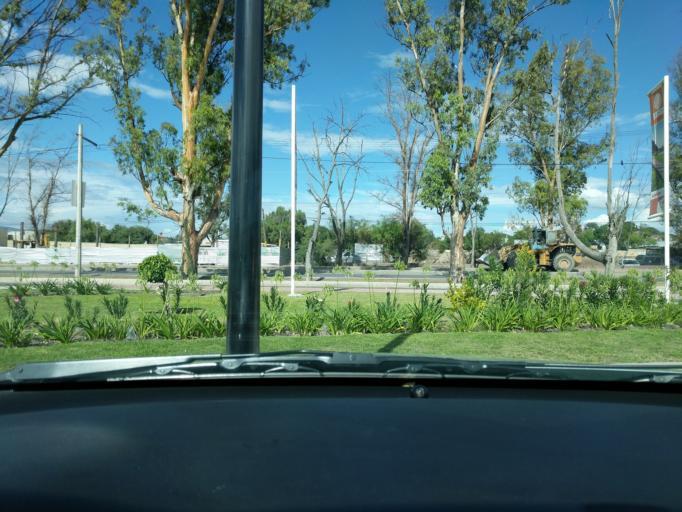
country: MX
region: Queretaro
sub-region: El Marques
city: Hacienda la Cruz [Fraccionamiento]
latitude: 20.6212
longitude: -100.2608
